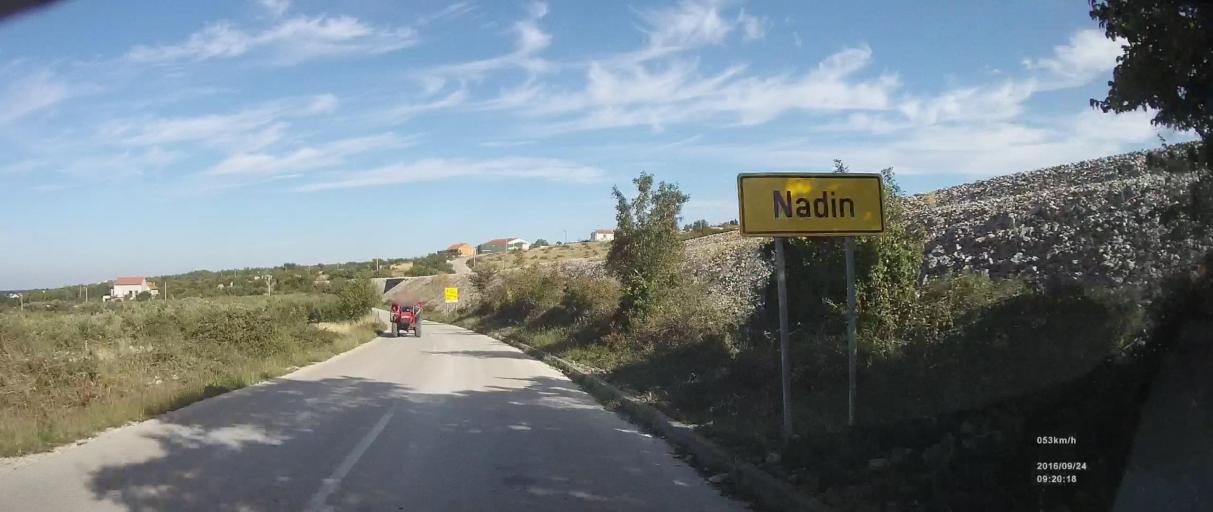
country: HR
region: Zadarska
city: Polaca
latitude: 44.0677
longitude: 15.4979
